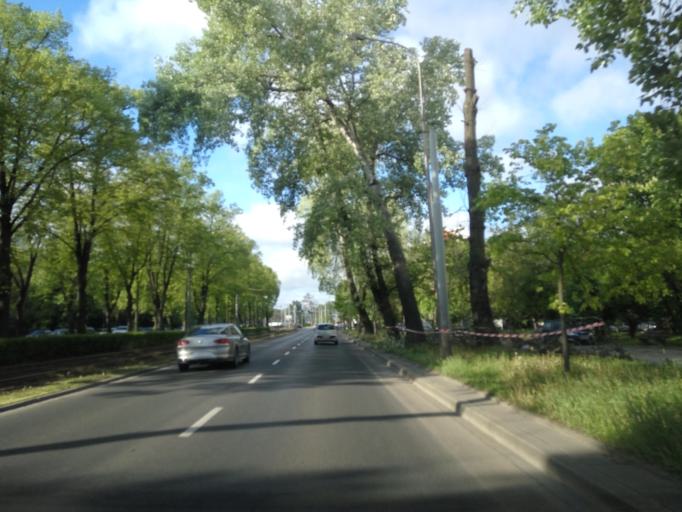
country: PL
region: Lower Silesian Voivodeship
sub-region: Powiat wroclawski
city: Wroclaw
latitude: 51.0818
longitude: 17.0088
